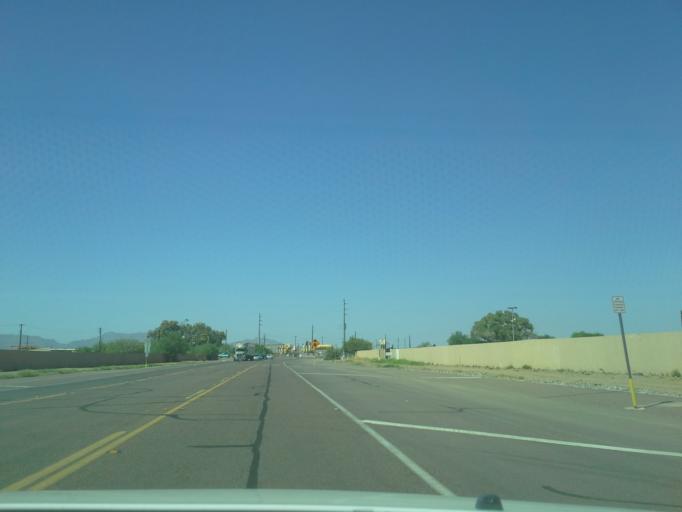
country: US
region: Arizona
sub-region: Maricopa County
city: Laveen
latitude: 33.4044
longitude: -112.1485
